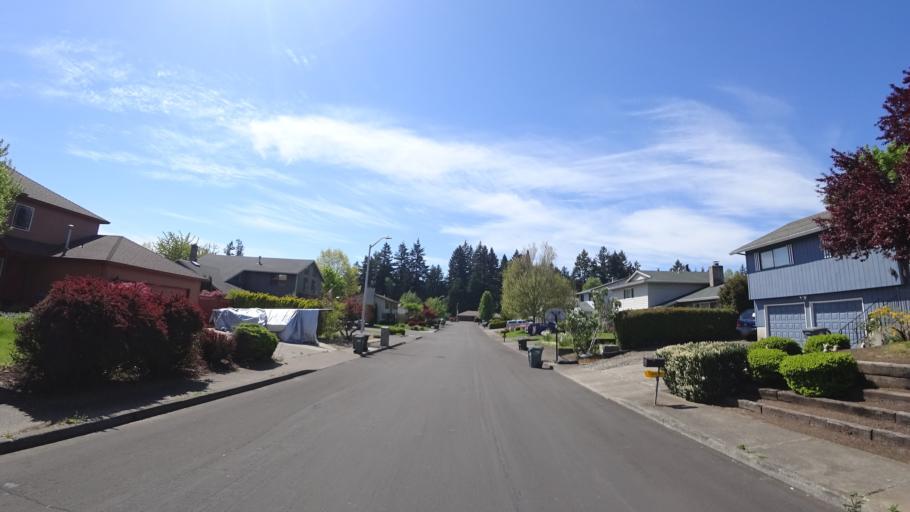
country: US
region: Oregon
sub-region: Washington County
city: Hillsboro
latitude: 45.5156
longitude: -122.9520
